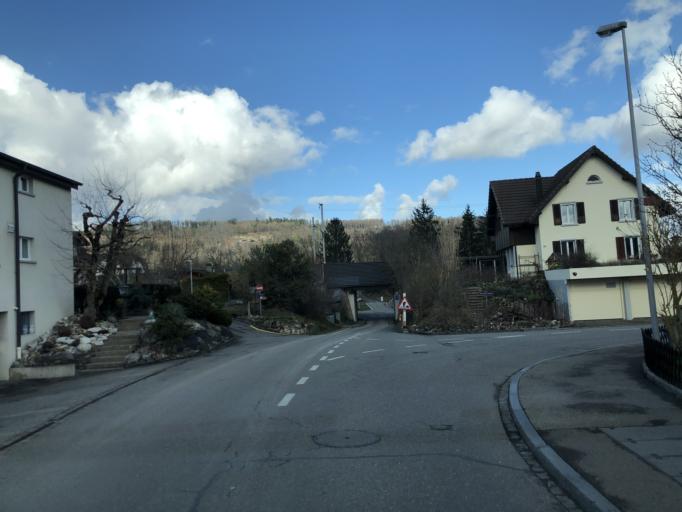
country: CH
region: Aargau
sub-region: Bezirk Brugg
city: Windisch
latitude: 47.4838
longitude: 8.2262
